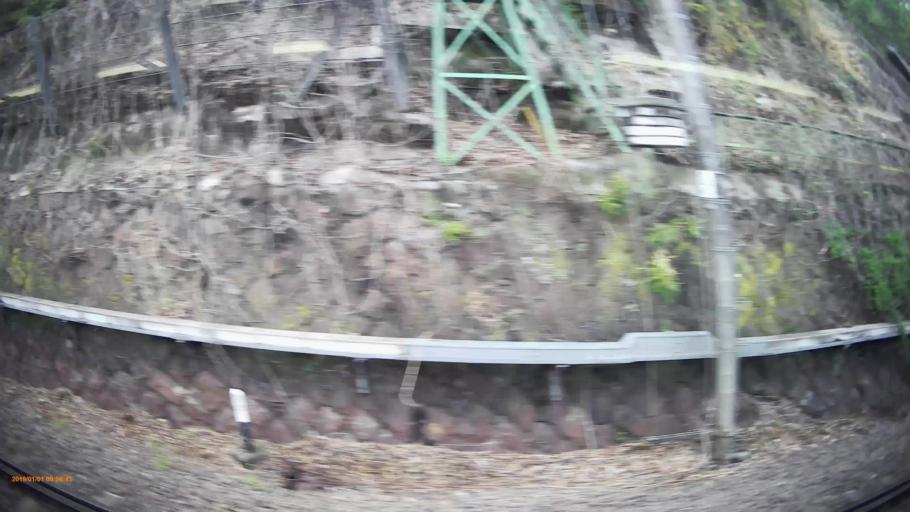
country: JP
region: Yamanashi
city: Otsuki
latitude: 35.6053
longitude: 138.8323
